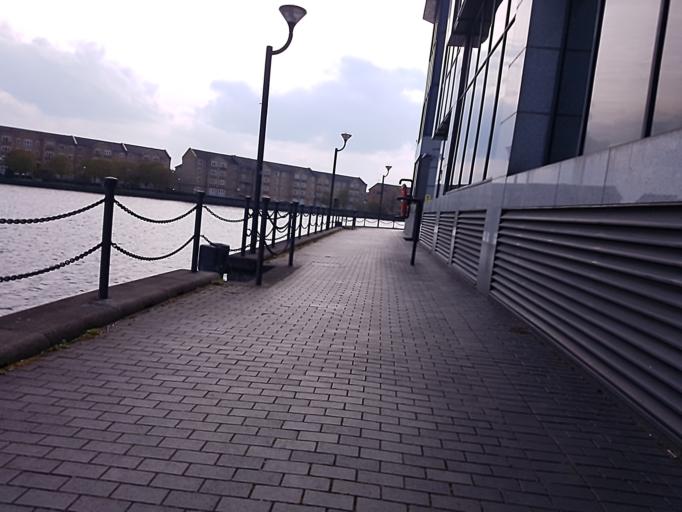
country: GB
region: England
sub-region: Greater London
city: Poplar
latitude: 51.4946
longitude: -0.0184
